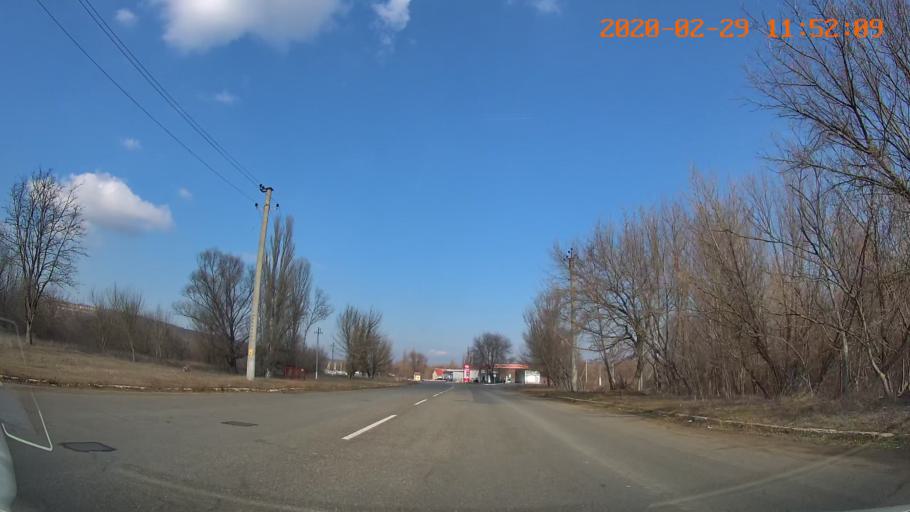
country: MD
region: Telenesti
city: Ribnita
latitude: 47.7702
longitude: 28.9913
